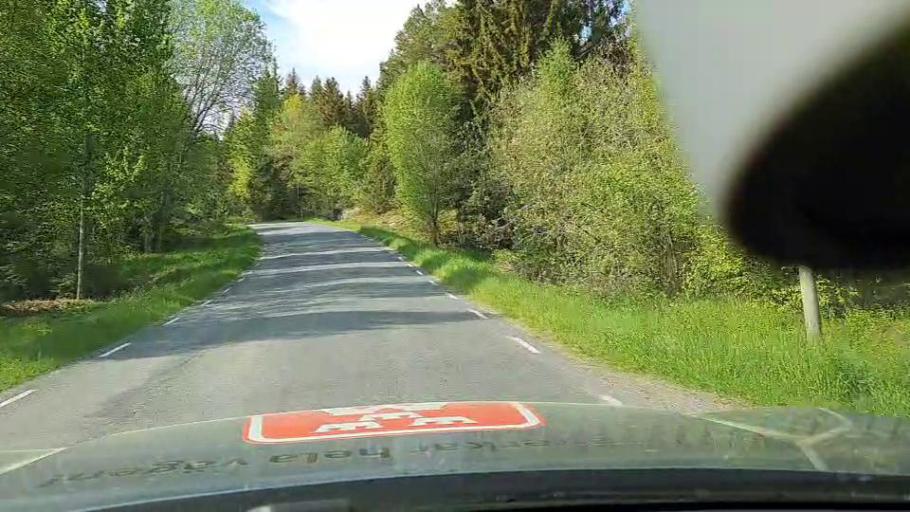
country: SE
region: Soedermanland
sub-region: Eskilstuna Kommun
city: Arla
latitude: 59.2632
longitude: 16.6552
